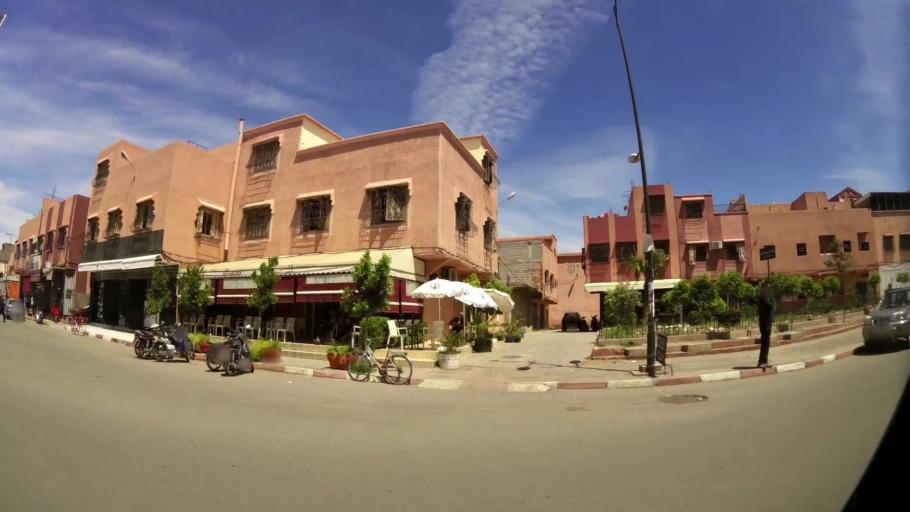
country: MA
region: Marrakech-Tensift-Al Haouz
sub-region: Marrakech
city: Marrakesh
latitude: 31.6600
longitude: -7.9968
